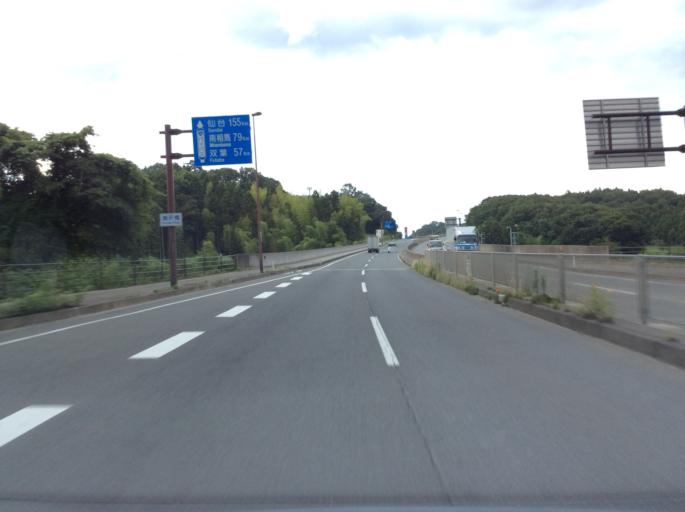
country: JP
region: Fukushima
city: Iwaki
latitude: 37.0222
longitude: 140.8942
